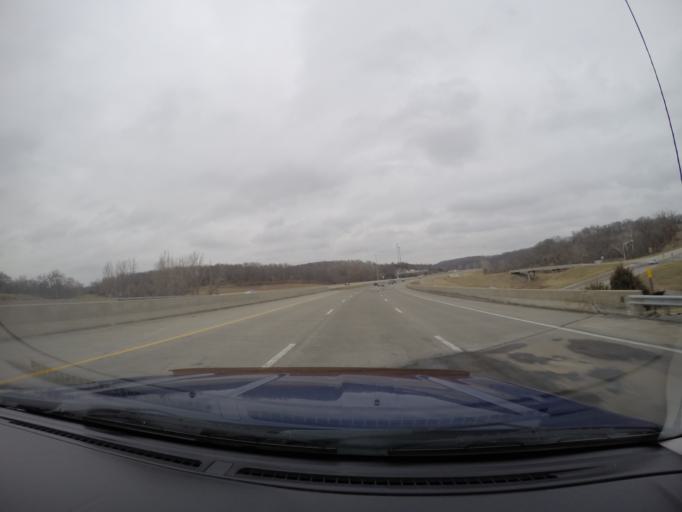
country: US
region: Kansas
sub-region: Wyandotte County
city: Edwardsville
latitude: 39.1580
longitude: -94.8204
